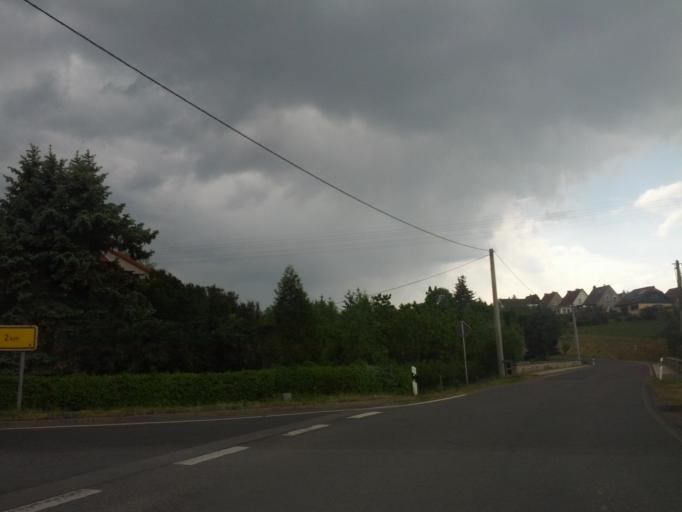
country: DE
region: Thuringia
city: Haina
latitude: 50.9897
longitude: 10.5246
